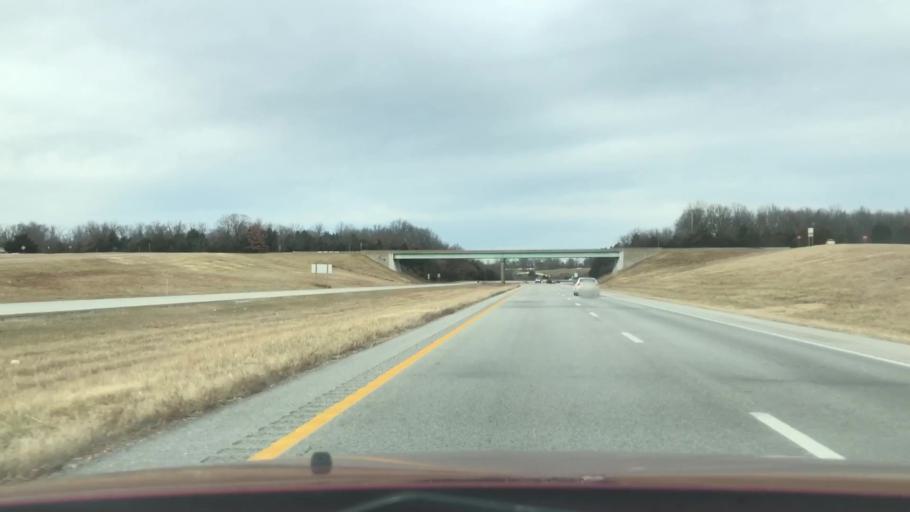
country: US
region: Missouri
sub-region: Greene County
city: Springfield
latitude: 37.2585
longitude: -93.2246
